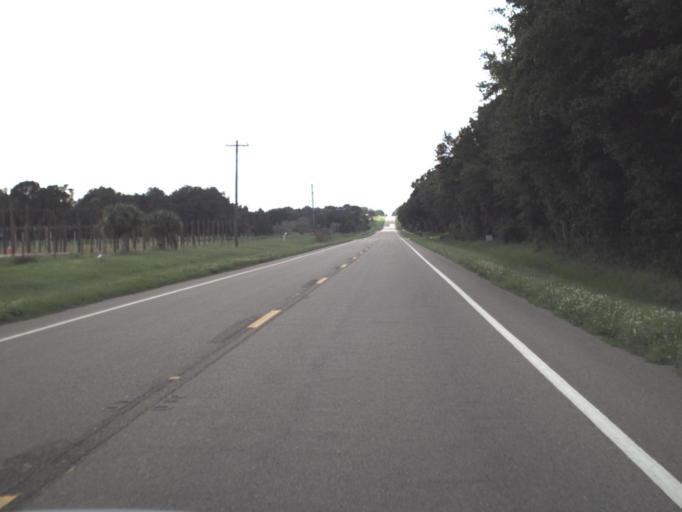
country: US
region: Florida
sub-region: Hardee County
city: Zolfo Springs
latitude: 27.4822
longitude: -81.8573
